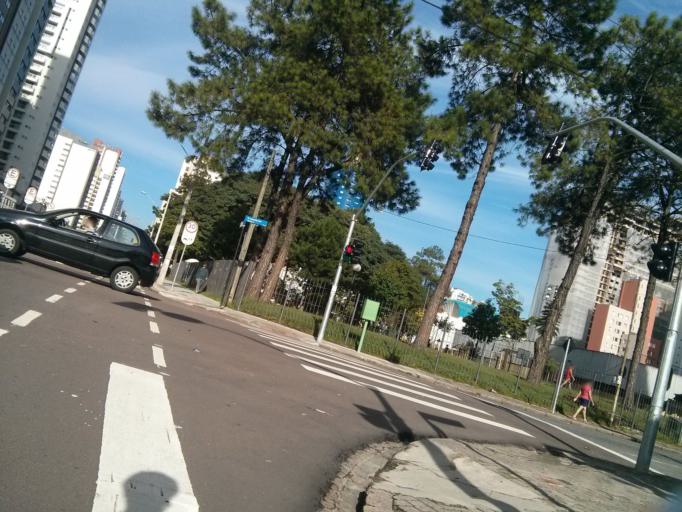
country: BR
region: Parana
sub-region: Curitiba
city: Curitiba
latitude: -25.4408
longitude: -49.2752
